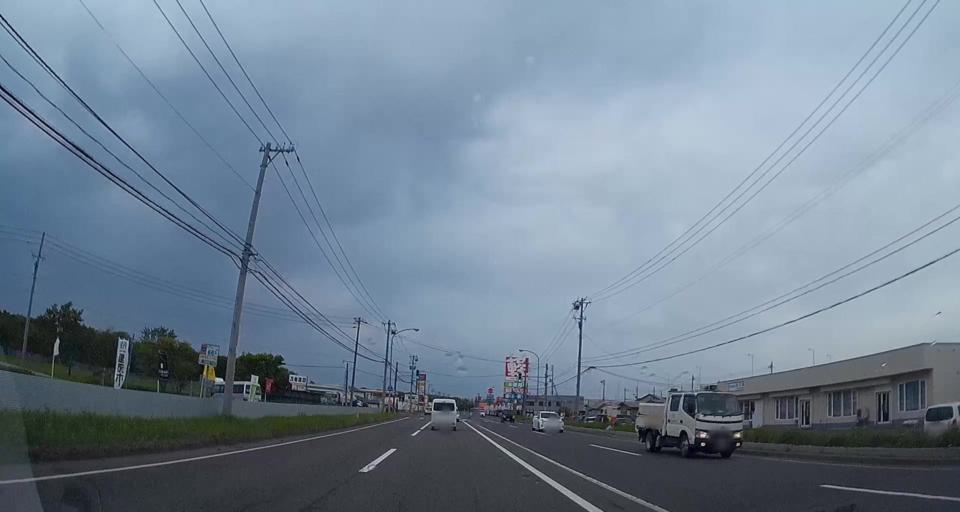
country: JP
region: Hokkaido
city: Tomakomai
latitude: 42.6738
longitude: 141.7066
